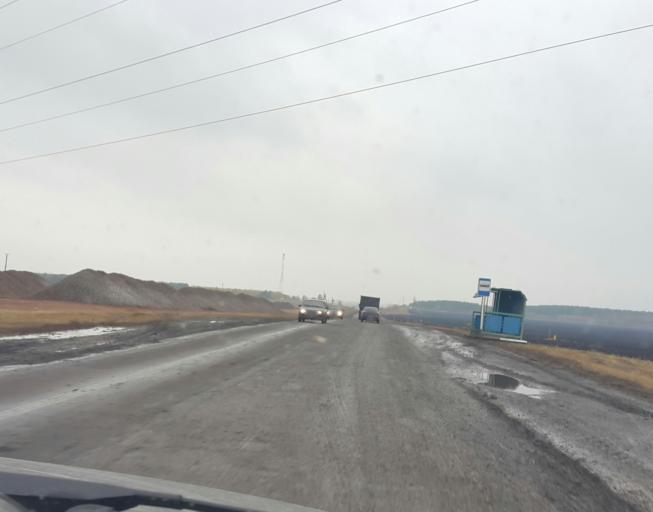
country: RU
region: Tambov
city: Znamenka
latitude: 52.4244
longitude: 41.5042
